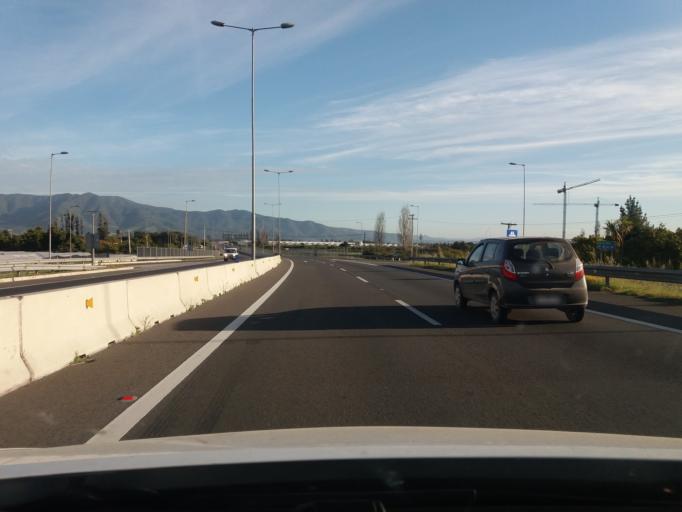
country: CL
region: Valparaiso
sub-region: Provincia de Quillota
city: Quillota
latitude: -32.8442
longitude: -71.2241
